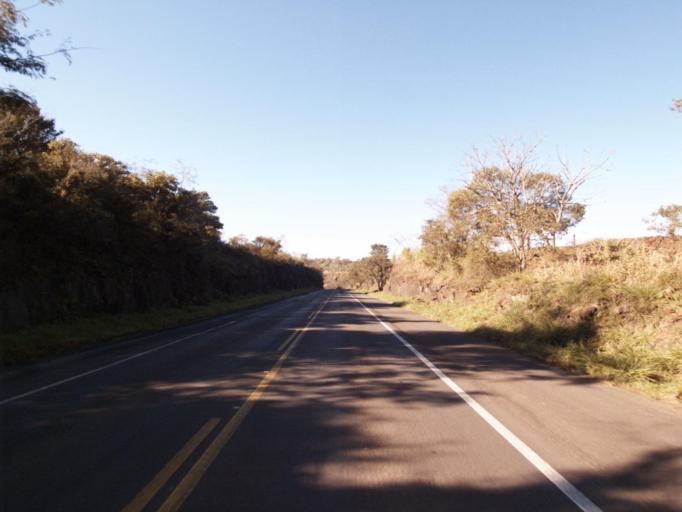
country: BR
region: Rio Grande do Sul
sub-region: Frederico Westphalen
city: Frederico Westphalen
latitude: -26.8103
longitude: -53.4386
